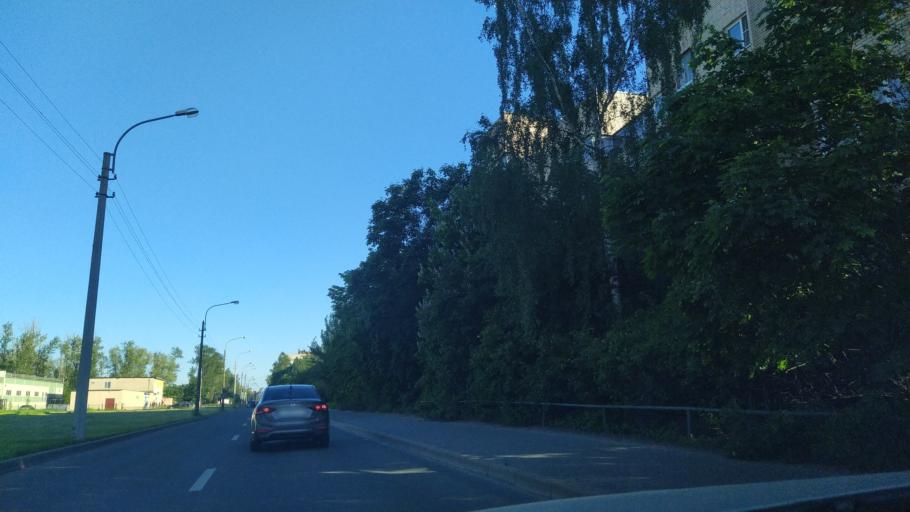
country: RU
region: St.-Petersburg
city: Pushkin
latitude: 59.7410
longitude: 30.4181
